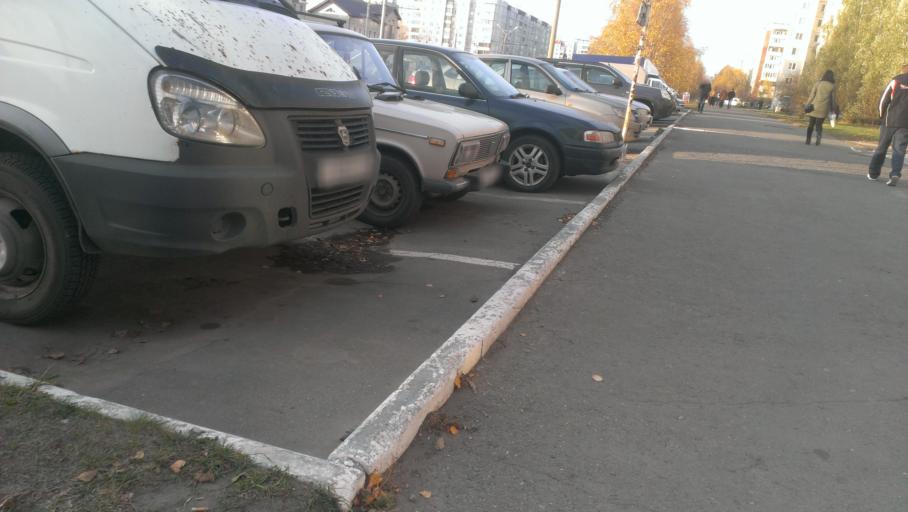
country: RU
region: Altai Krai
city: Novosilikatnyy
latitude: 53.3373
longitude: 83.6698
